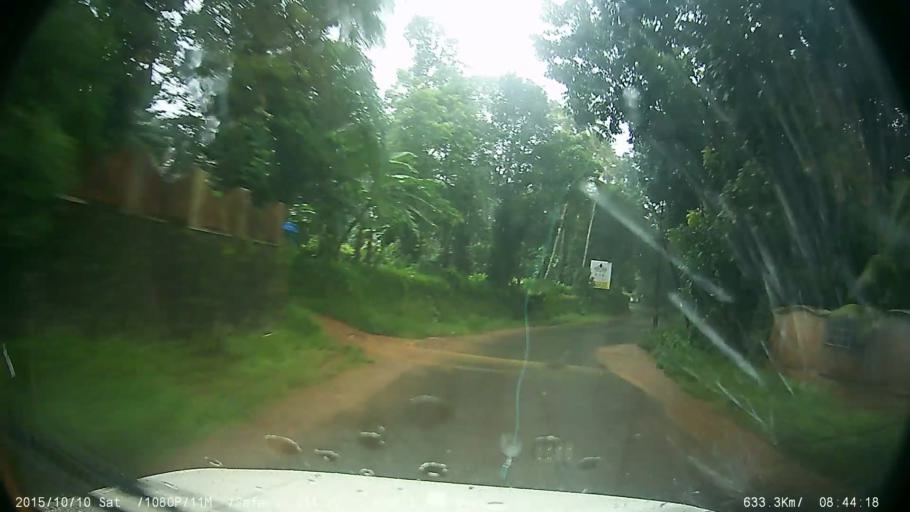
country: IN
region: Kerala
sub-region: Kottayam
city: Palackattumala
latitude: 9.7442
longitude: 76.5281
